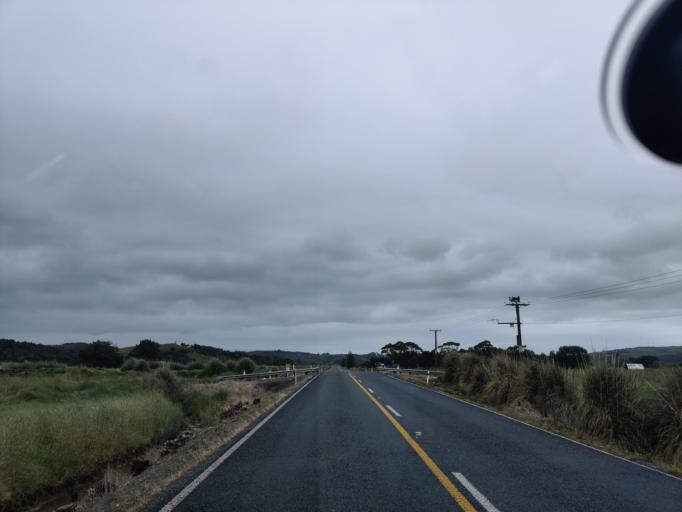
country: NZ
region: Northland
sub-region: Kaipara District
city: Dargaville
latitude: -36.1191
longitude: 174.0744
